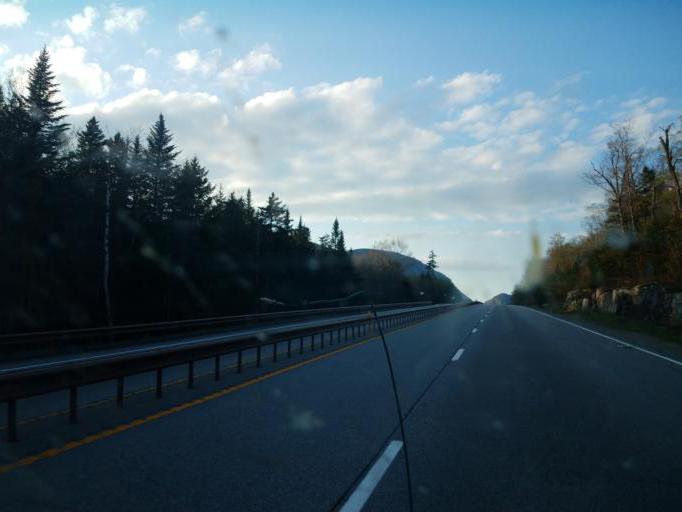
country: US
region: New Hampshire
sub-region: Grafton County
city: Deerfield
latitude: 44.1210
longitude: -71.6820
